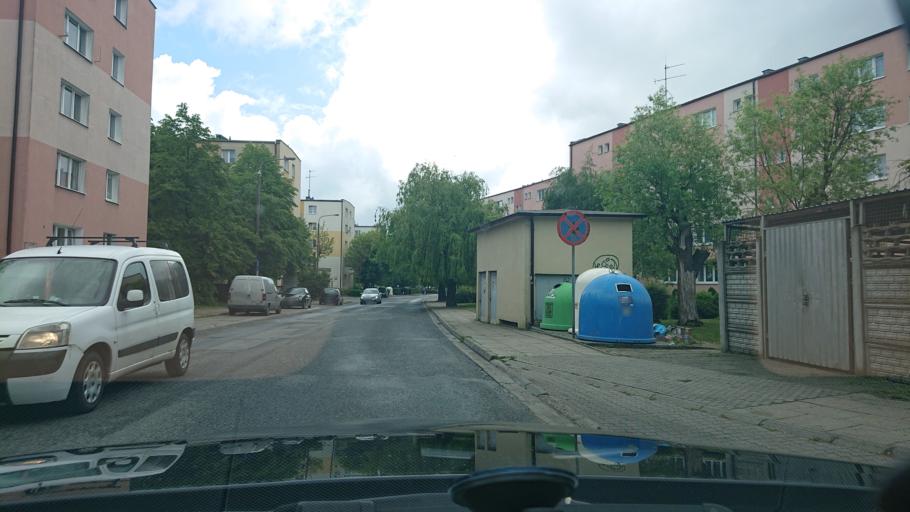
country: PL
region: Greater Poland Voivodeship
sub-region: Powiat gnieznienski
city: Gniezno
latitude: 52.5426
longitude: 17.6156
